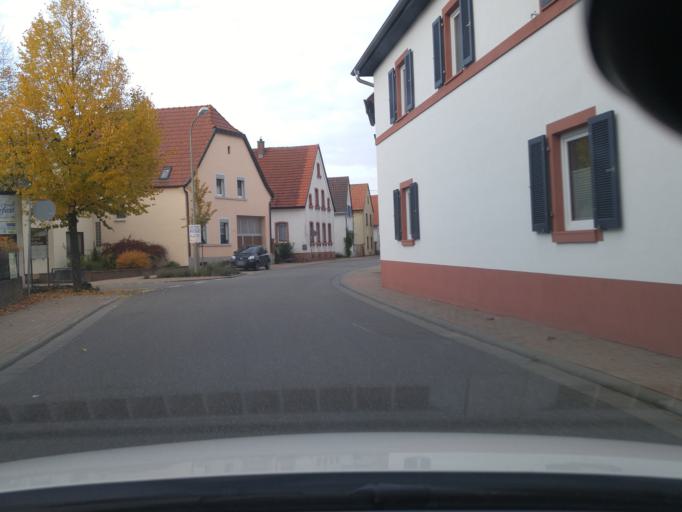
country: DE
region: Rheinland-Pfalz
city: Dudenhofen
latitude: 49.2867
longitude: 8.3986
